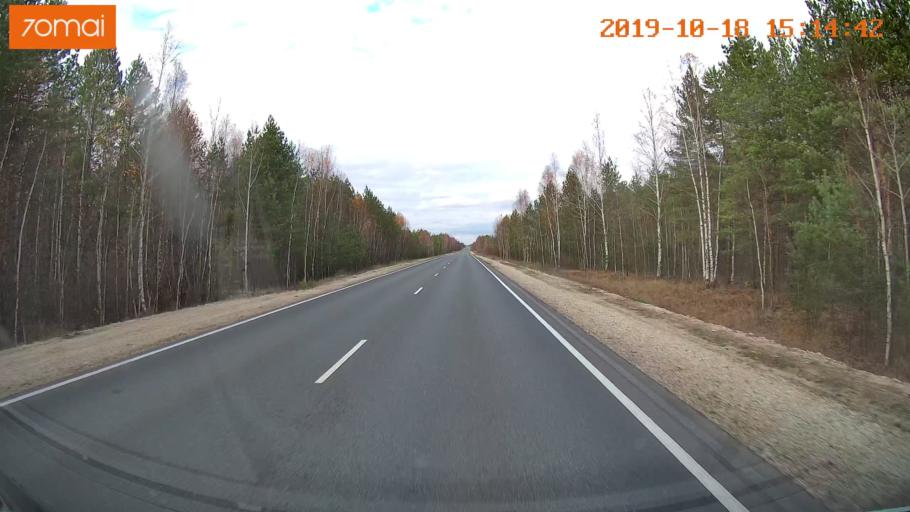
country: RU
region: Vladimir
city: Gus'-Khrustal'nyy
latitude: 55.6069
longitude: 40.7208
